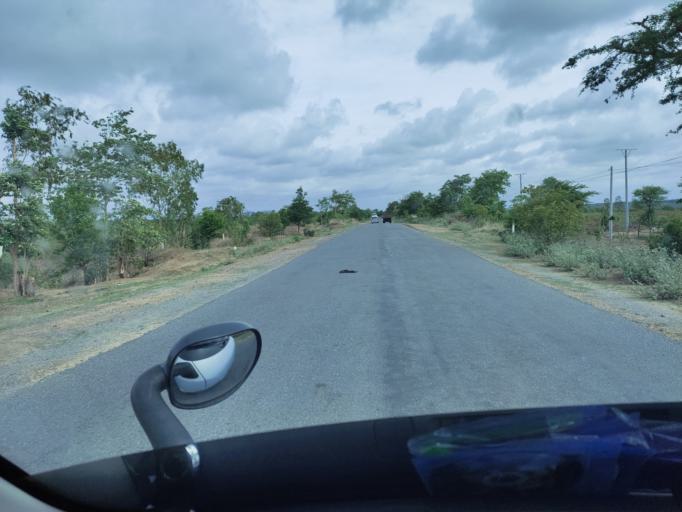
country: MM
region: Magway
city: Chauk
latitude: 20.9765
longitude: 95.0516
